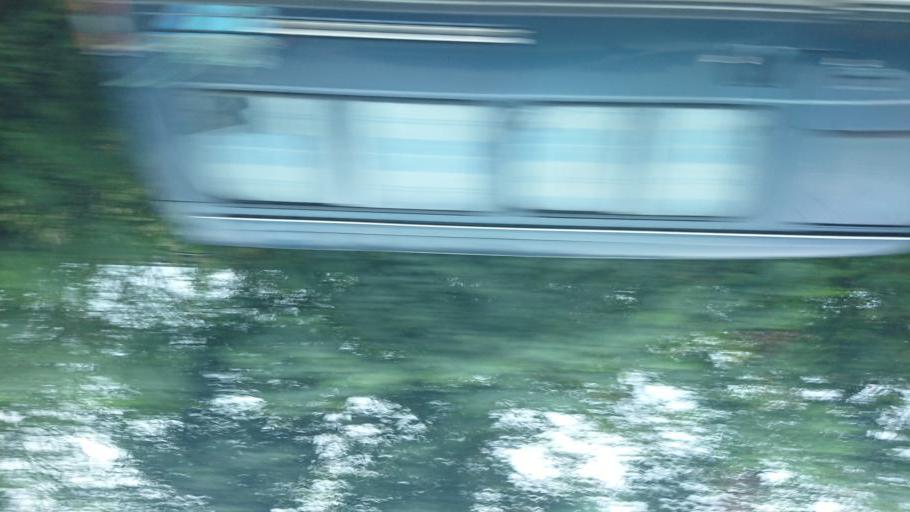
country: TW
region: Taiwan
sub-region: Hsinchu
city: Hsinchu
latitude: 24.8393
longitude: 120.9427
